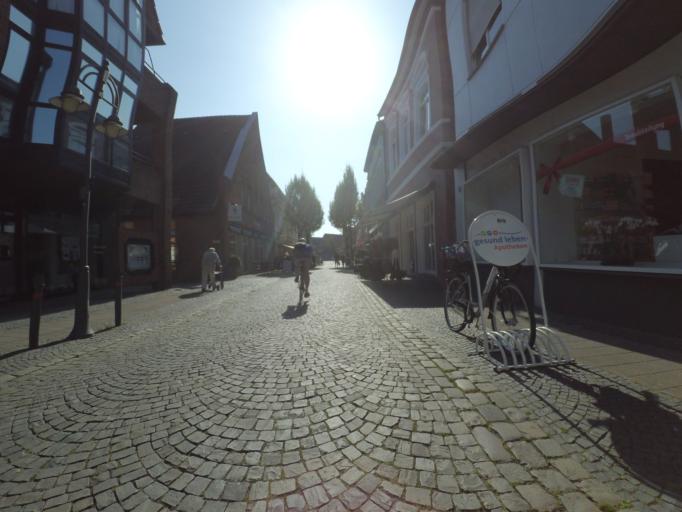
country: DE
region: North Rhine-Westphalia
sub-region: Regierungsbezirk Munster
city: Steinfurt
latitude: 52.1489
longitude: 7.3370
